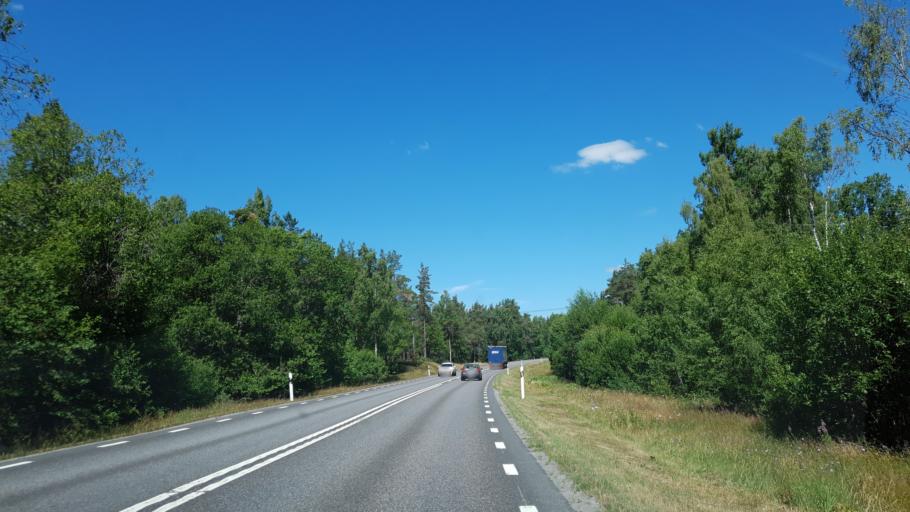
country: SE
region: Joenkoeping
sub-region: Varnamo Kommun
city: Rydaholm
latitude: 57.0060
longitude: 14.2642
